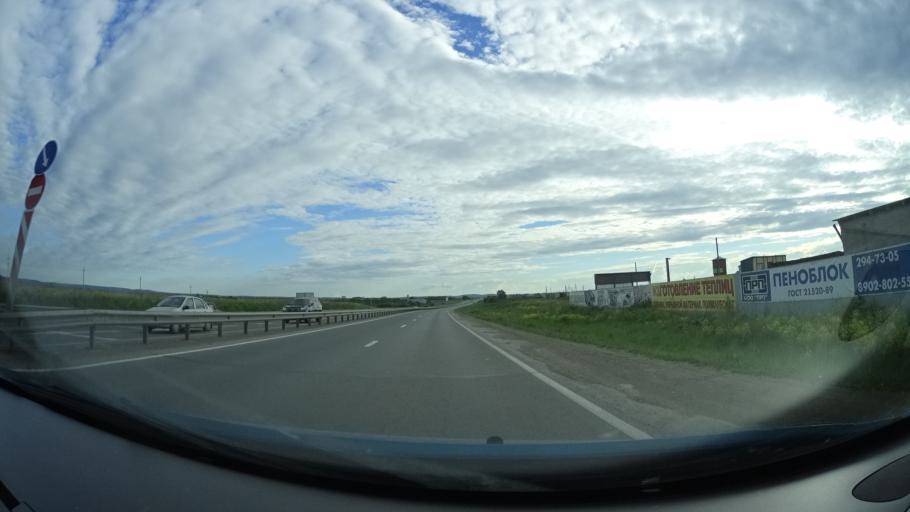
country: RU
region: Perm
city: Kultayevo
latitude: 57.9078
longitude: 55.9892
